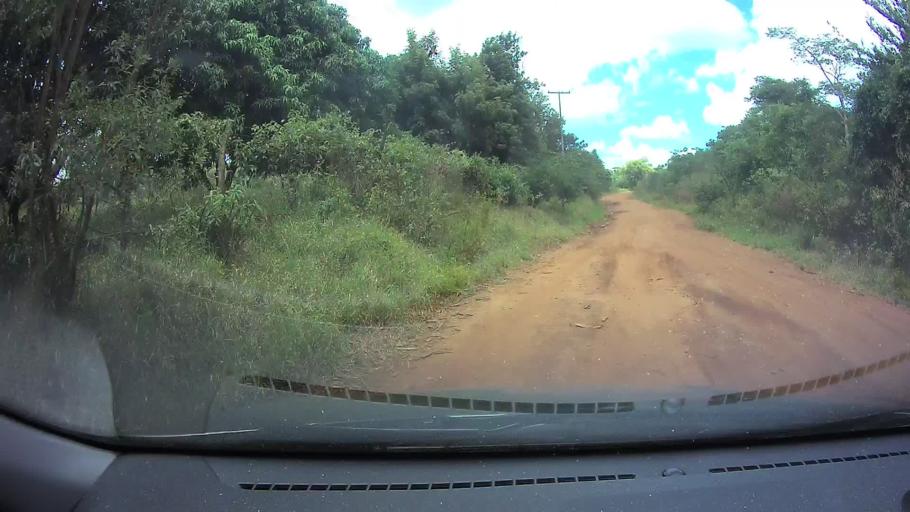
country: PY
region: Paraguari
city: La Colmena
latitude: -25.9309
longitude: -56.7842
